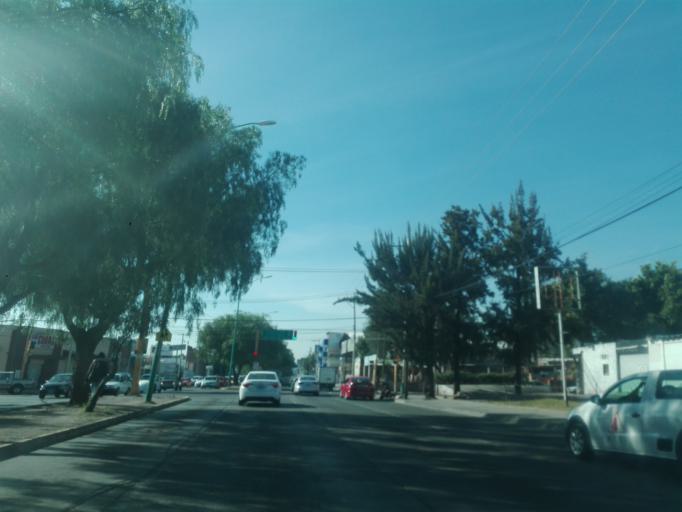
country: MX
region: Guanajuato
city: Leon
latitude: 21.1060
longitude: -101.6549
